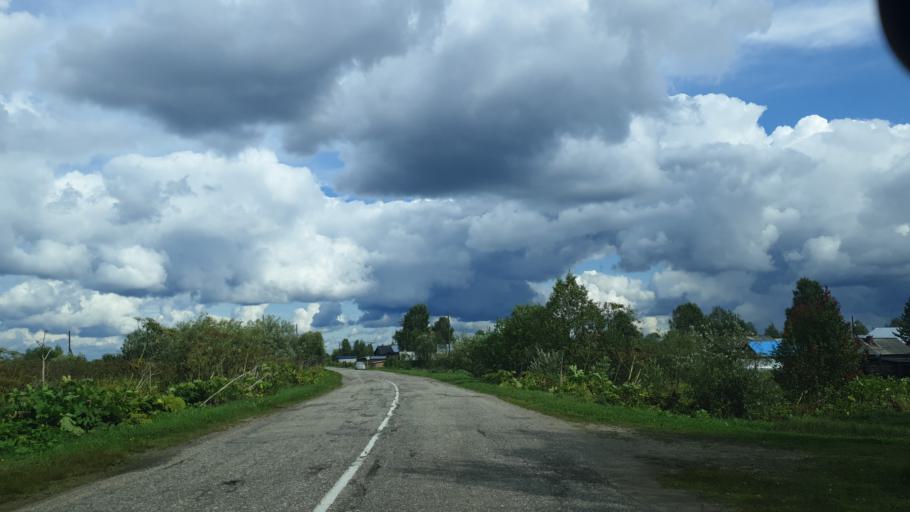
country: RU
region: Komi Republic
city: Aykino
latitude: 61.9532
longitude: 50.1765
